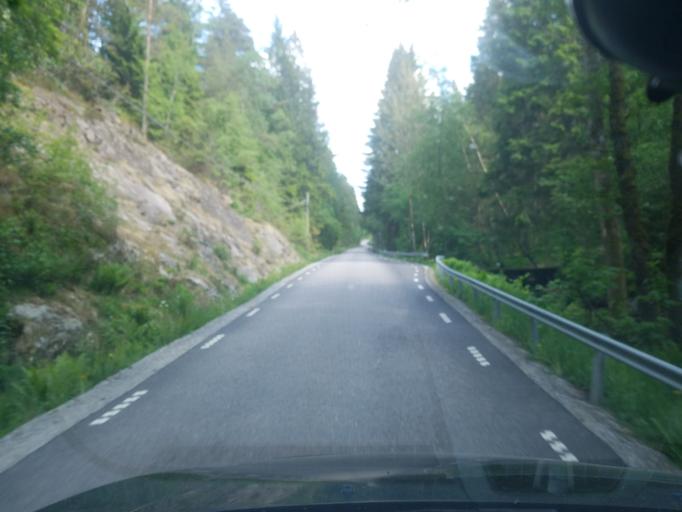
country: SE
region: Vaestra Goetaland
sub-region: Stenungsunds Kommun
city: Stora Hoga
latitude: 58.0167
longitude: 11.9035
